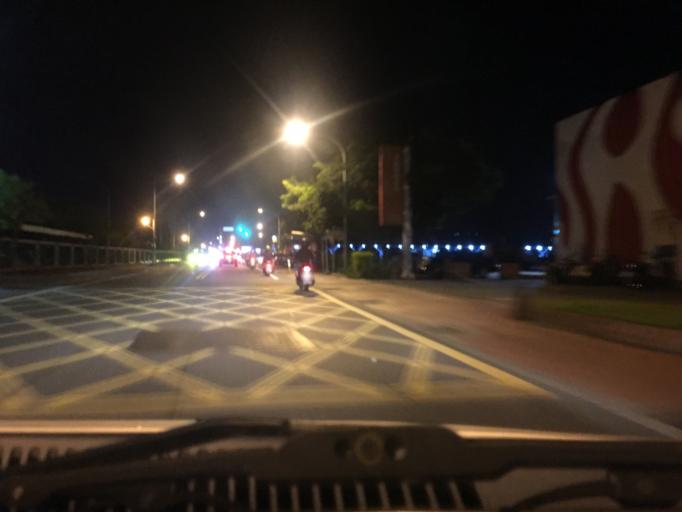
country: TW
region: Taiwan
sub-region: Yilan
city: Yilan
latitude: 24.7510
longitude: 121.7581
